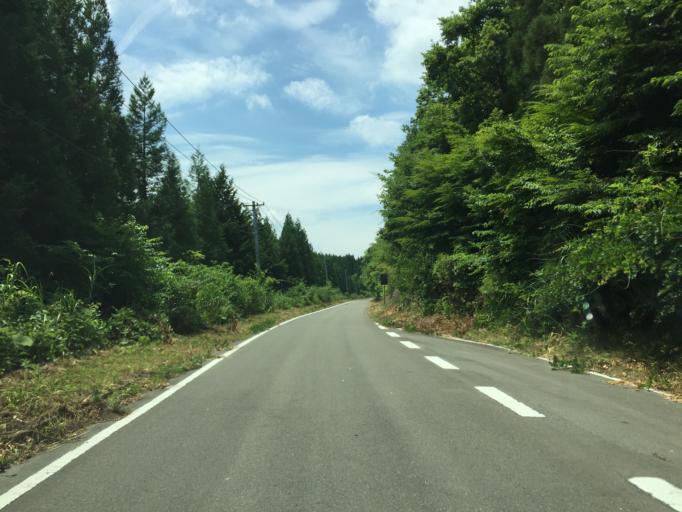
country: JP
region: Miyagi
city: Marumori
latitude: 37.7528
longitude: 140.7356
